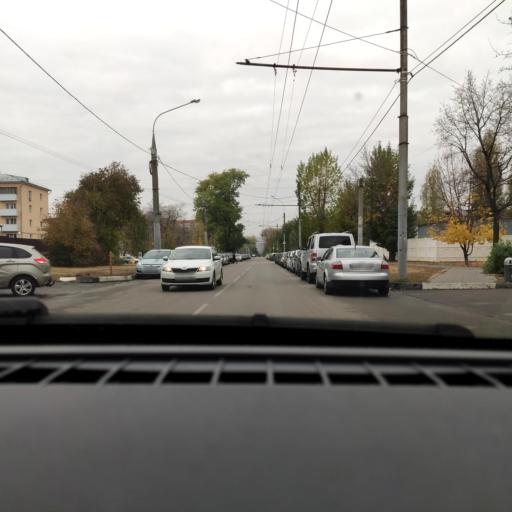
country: RU
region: Voronezj
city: Voronezh
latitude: 51.6374
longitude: 39.2456
